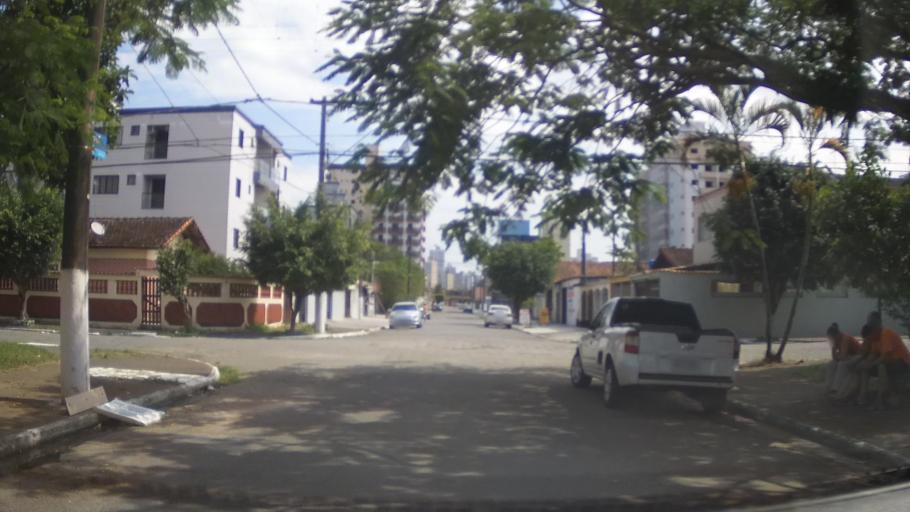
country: BR
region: Sao Paulo
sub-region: Praia Grande
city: Praia Grande
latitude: -24.0107
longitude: -46.4299
